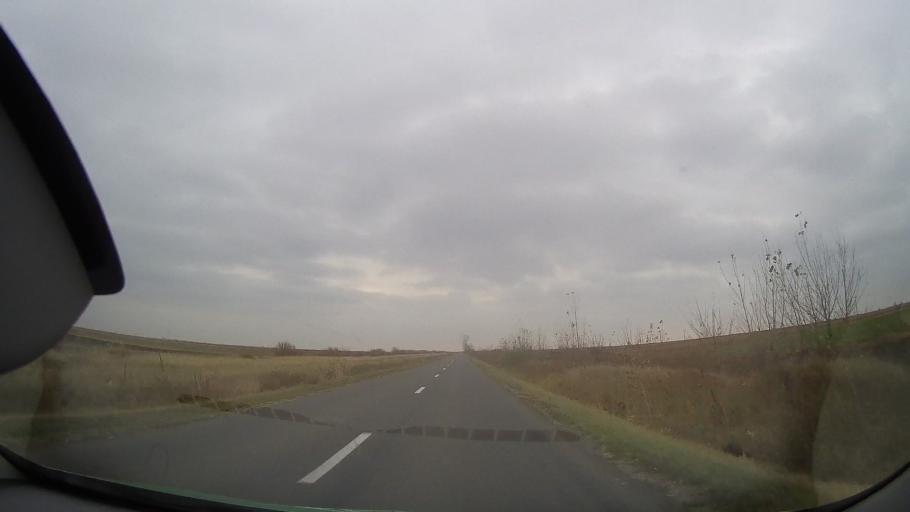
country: RO
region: Ialomita
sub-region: Comuna Garbovi
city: Garbovi
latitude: 44.7657
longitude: 26.7379
